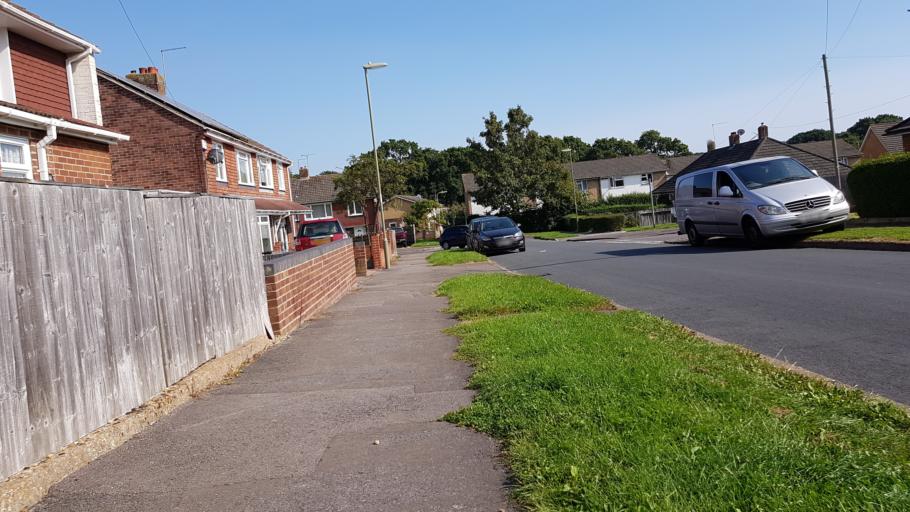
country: GB
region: England
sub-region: Hampshire
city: Waterlooville
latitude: 50.8715
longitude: -1.0337
